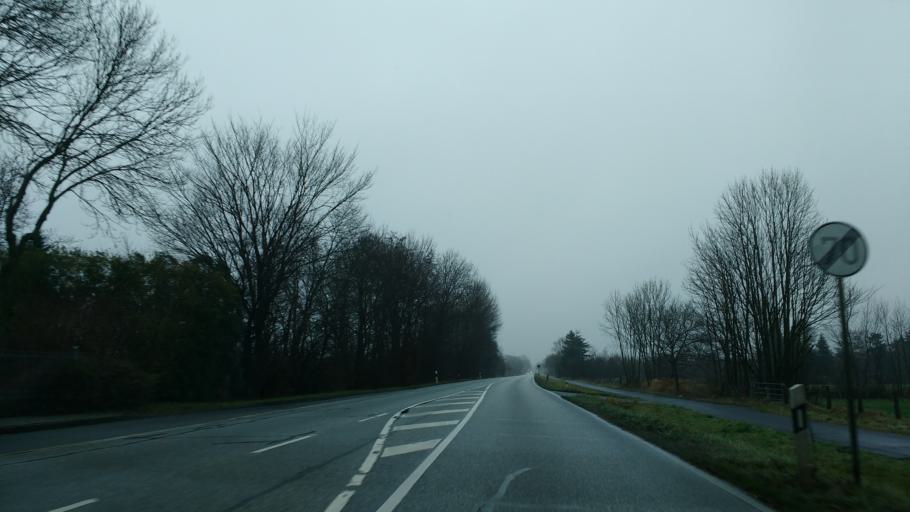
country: DE
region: Schleswig-Holstein
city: Brinjahe
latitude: 54.1842
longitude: 9.6375
